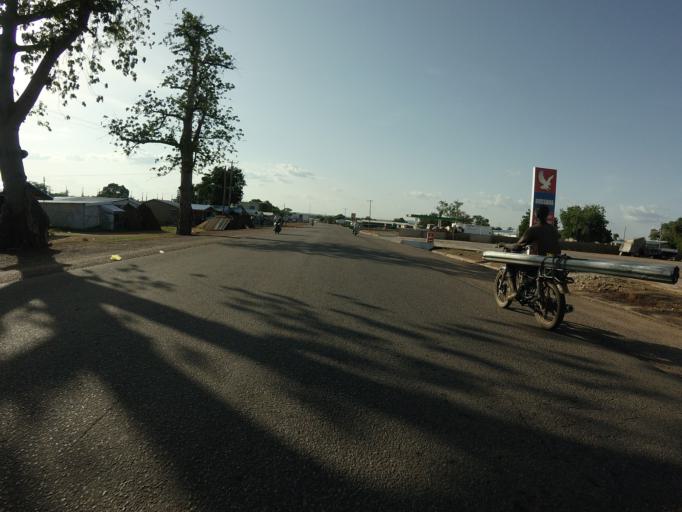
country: GH
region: Upper East
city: Navrongo
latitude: 10.9824
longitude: -1.1068
